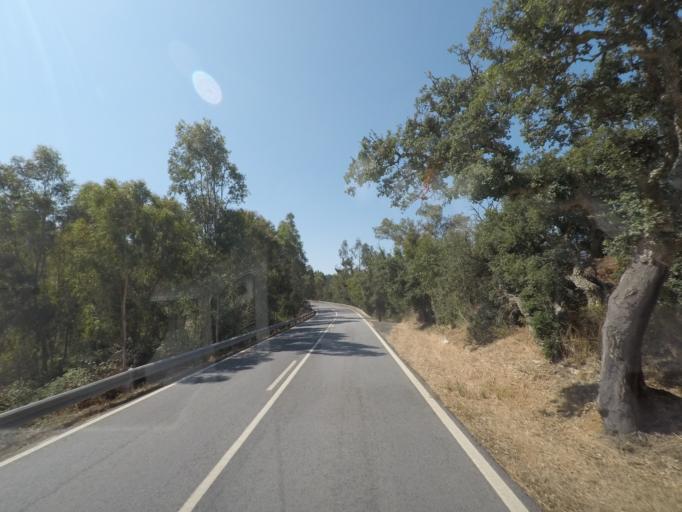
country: PT
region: Beja
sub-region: Odemira
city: Sao Teotonio
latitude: 37.5336
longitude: -8.6945
